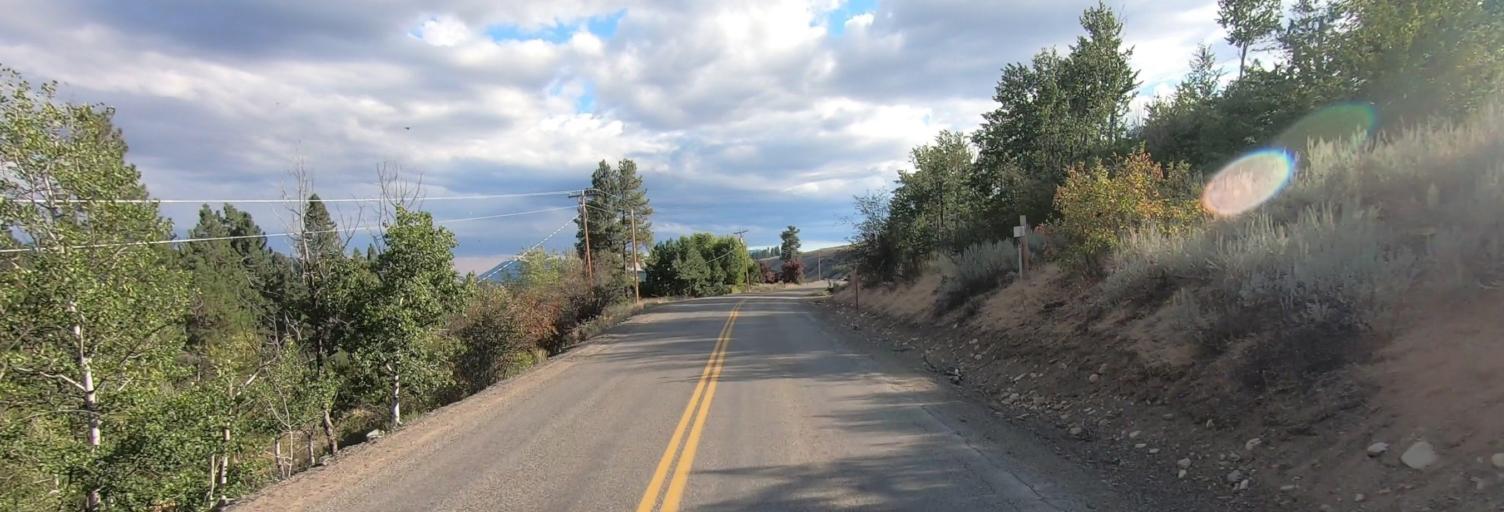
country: US
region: Washington
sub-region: Okanogan County
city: Brewster
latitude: 48.5218
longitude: -120.1912
